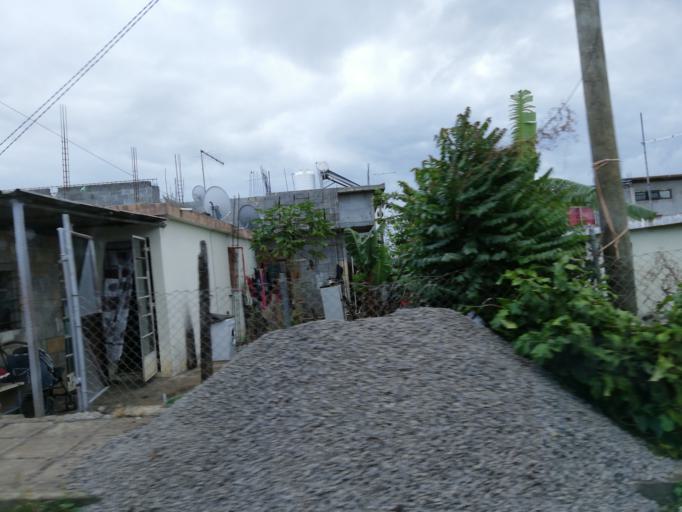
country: MU
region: Black River
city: Petite Riviere
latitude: -20.2114
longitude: 57.4639
